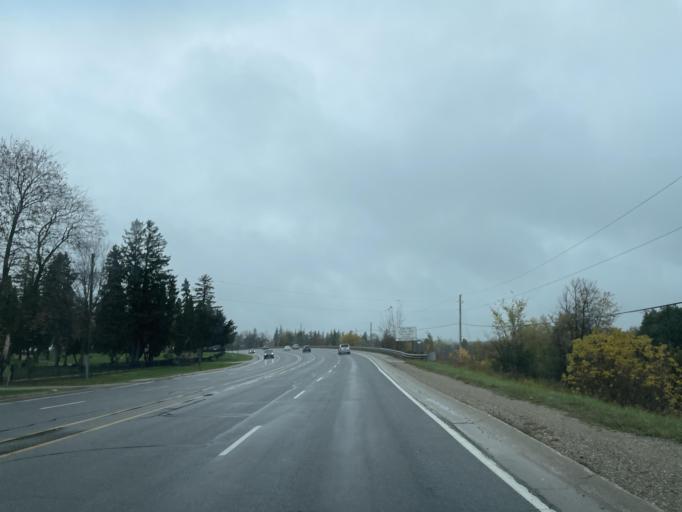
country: CA
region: Ontario
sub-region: Wellington County
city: Guelph
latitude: 43.5687
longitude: -80.2789
